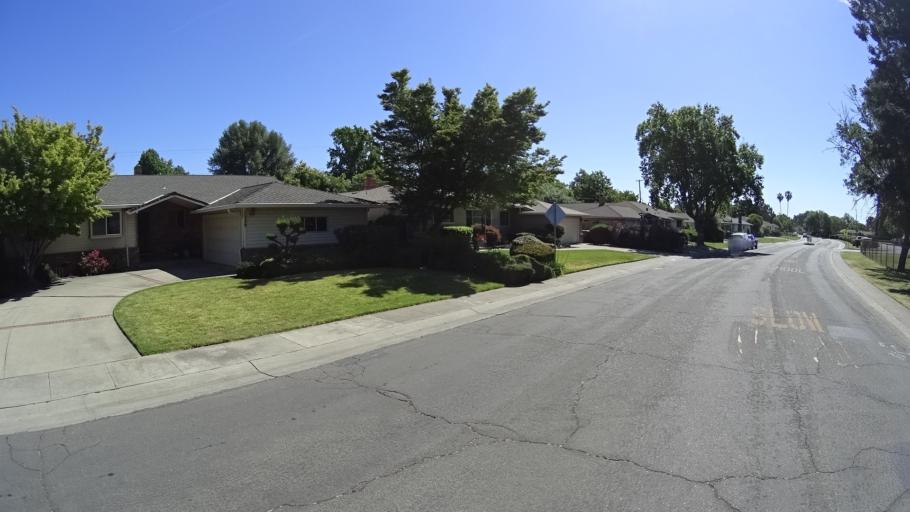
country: US
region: California
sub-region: Sacramento County
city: Parkway
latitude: 38.5014
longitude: -121.5126
